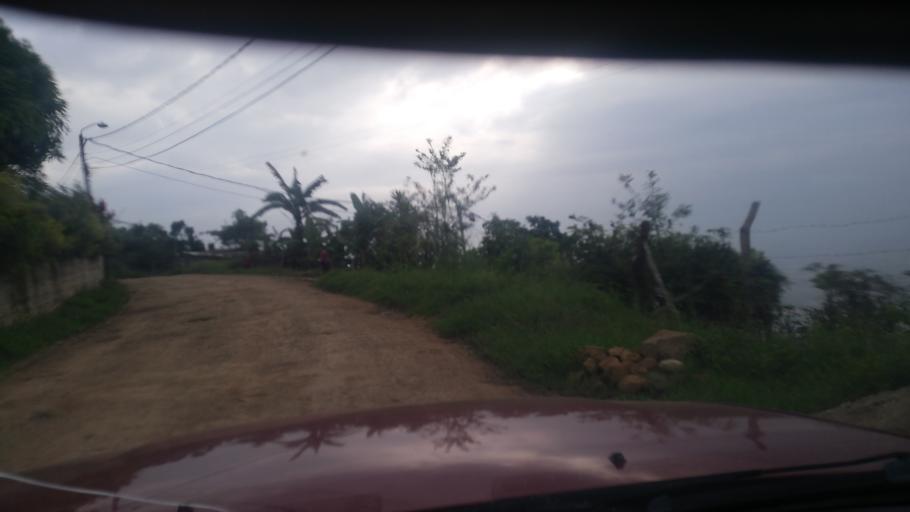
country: CO
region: Valle del Cauca
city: Cali
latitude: 3.5047
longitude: -76.5453
